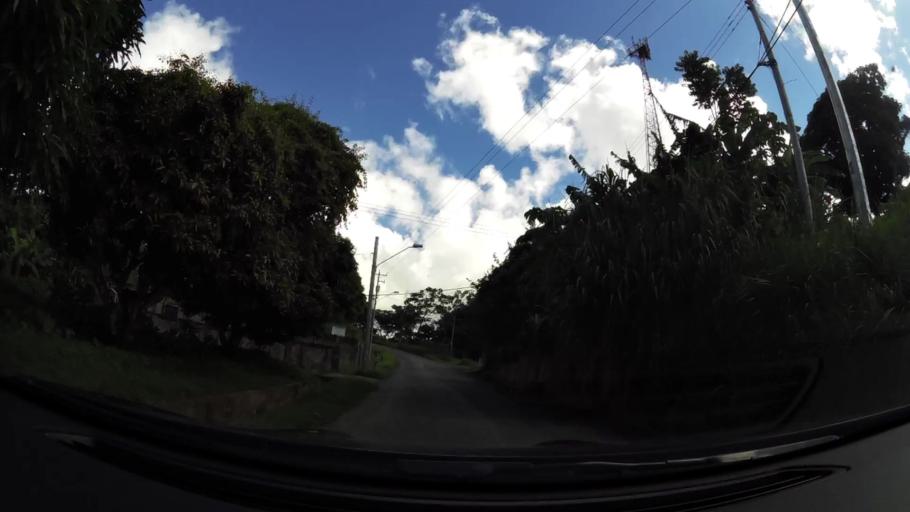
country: TT
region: Eastern Tobago
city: Roxborough
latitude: 11.3093
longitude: -60.6199
